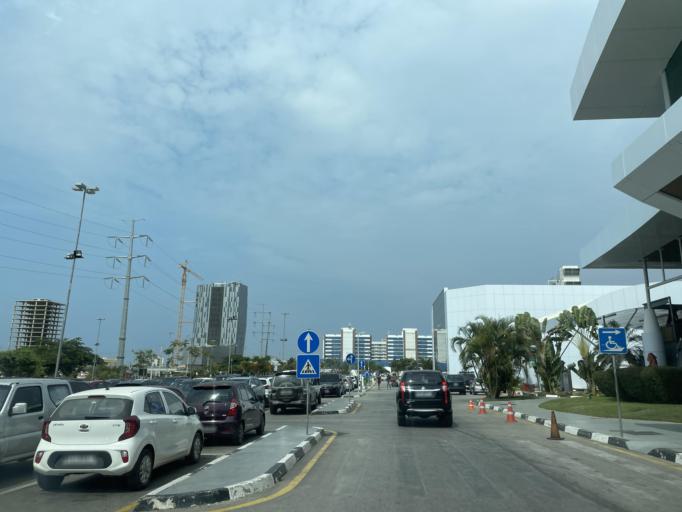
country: AO
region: Luanda
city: Luanda
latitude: -8.9243
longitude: 13.1846
